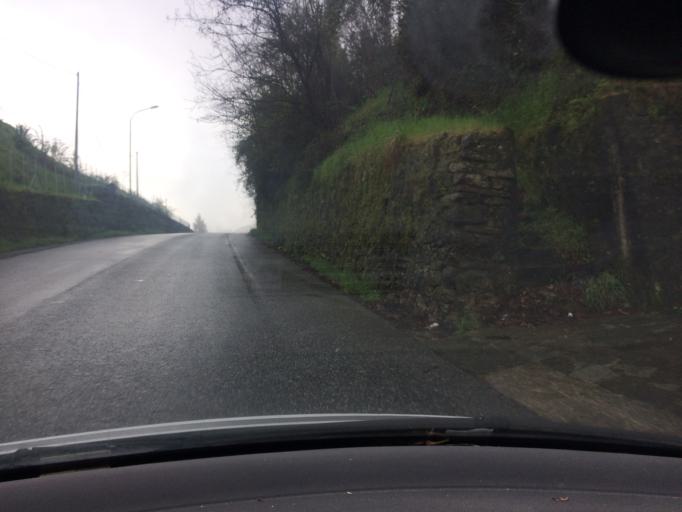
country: IT
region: Tuscany
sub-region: Provincia di Massa-Carrara
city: Massa
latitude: 44.0669
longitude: 10.1105
